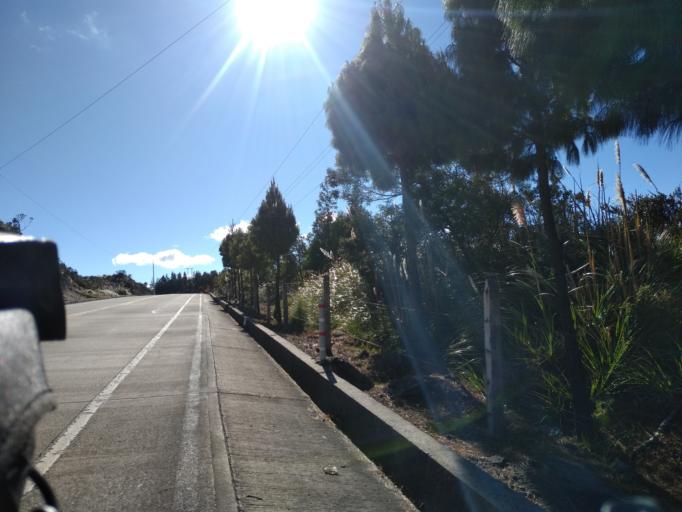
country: EC
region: Azuay
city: Cuenca
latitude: -3.3076
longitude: -79.1286
